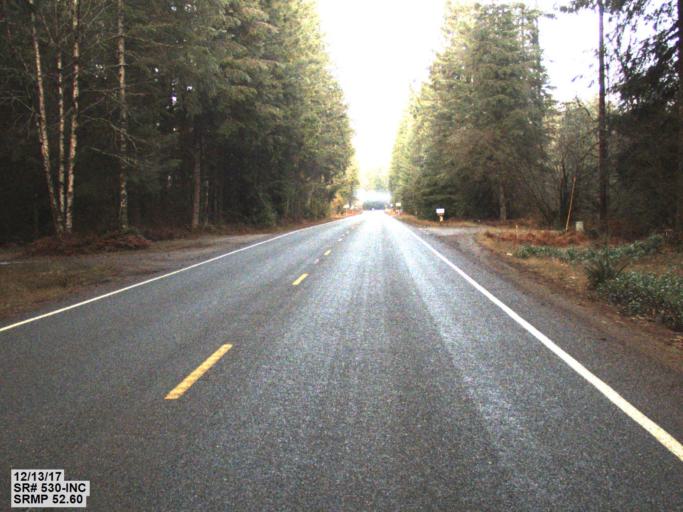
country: US
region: Washington
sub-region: Snohomish County
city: Darrington
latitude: 48.2953
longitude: -121.5625
